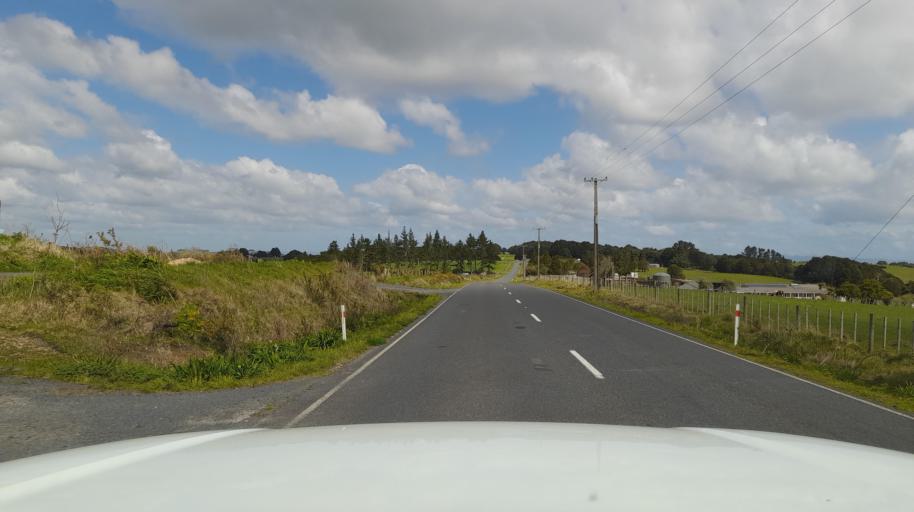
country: NZ
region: Northland
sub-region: Far North District
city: Waimate North
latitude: -35.2840
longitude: 173.8287
